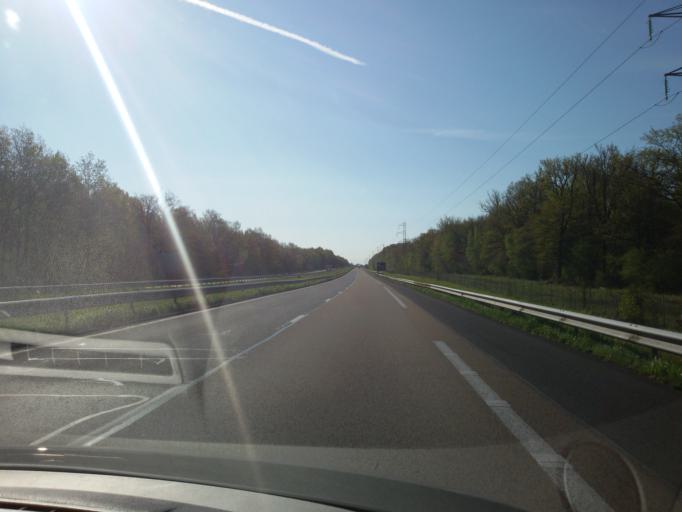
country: FR
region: Centre
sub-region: Departement du Loiret
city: Courtenay
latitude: 48.0815
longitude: 3.0512
